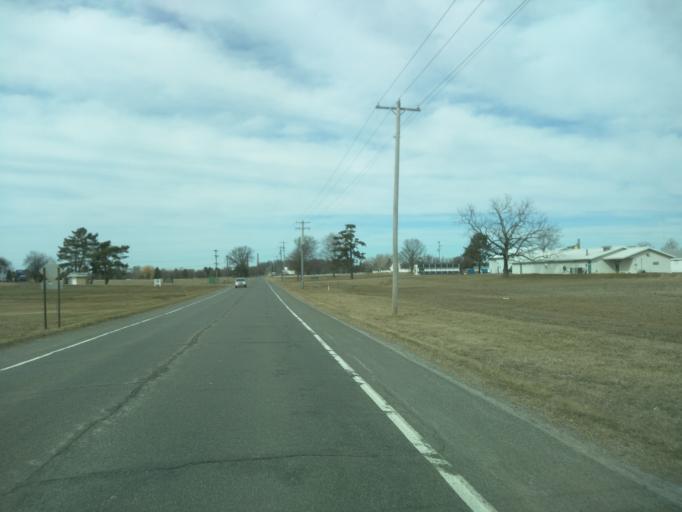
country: US
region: Michigan
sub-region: Ingham County
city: East Lansing
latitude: 42.6983
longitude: -84.4840
